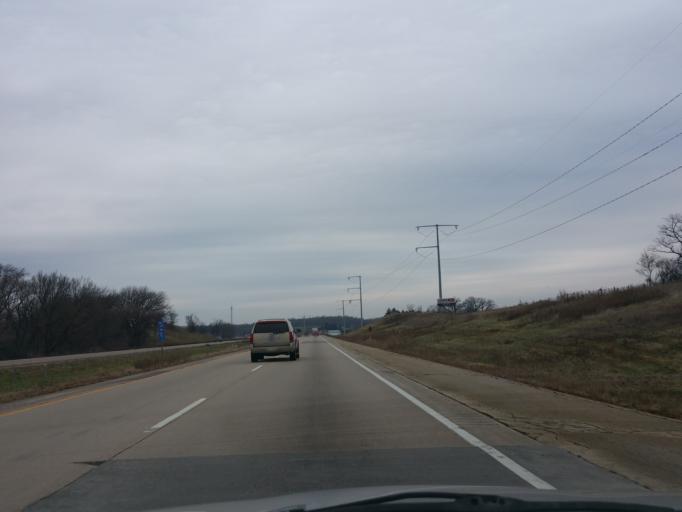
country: US
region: Wisconsin
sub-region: Dane County
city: Deerfield
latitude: 42.9873
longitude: -89.1315
